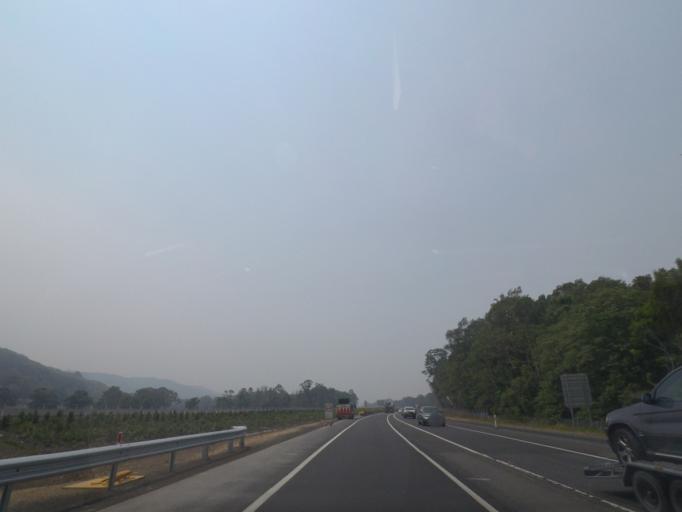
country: AU
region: New South Wales
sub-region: Ballina
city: Ballina
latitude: -28.9171
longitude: 153.4771
